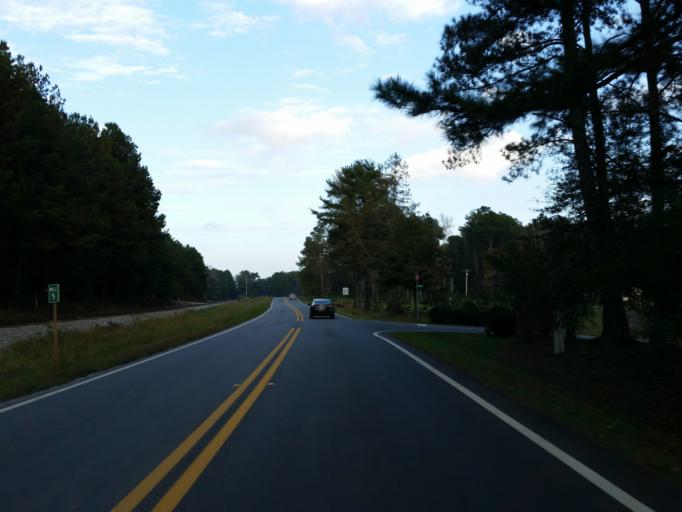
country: US
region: Georgia
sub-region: Monroe County
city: Forsyth
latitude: 32.9449
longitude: -83.8363
